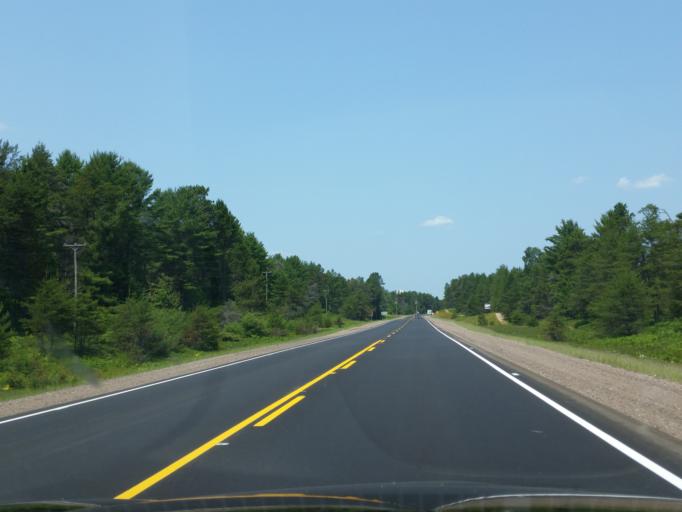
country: CA
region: Ontario
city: Deep River
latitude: 46.0095
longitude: -77.4358
